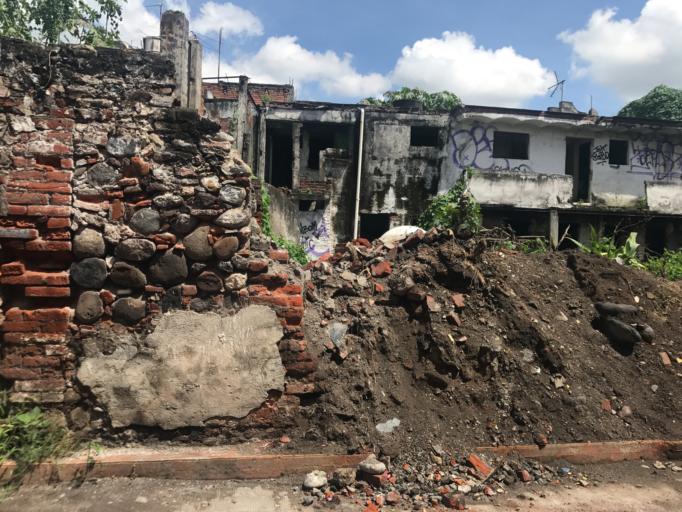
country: MX
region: Morelos
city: Cuautla Morelos
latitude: 18.8152
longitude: -98.9561
